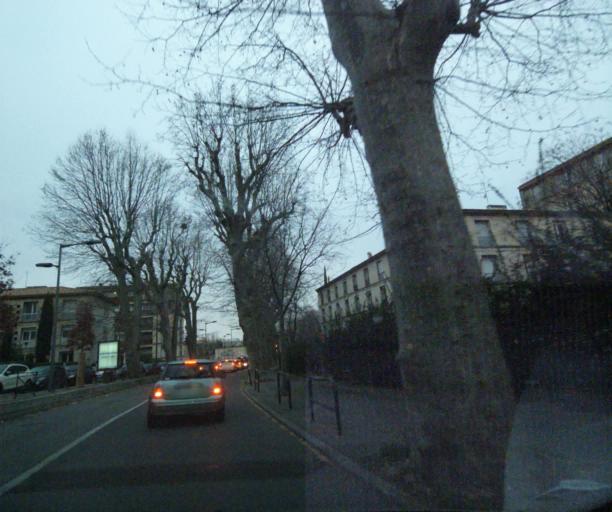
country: FR
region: Provence-Alpes-Cote d'Azur
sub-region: Departement des Bouches-du-Rhone
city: Aix-en-Provence
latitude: 43.5334
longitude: 5.4565
